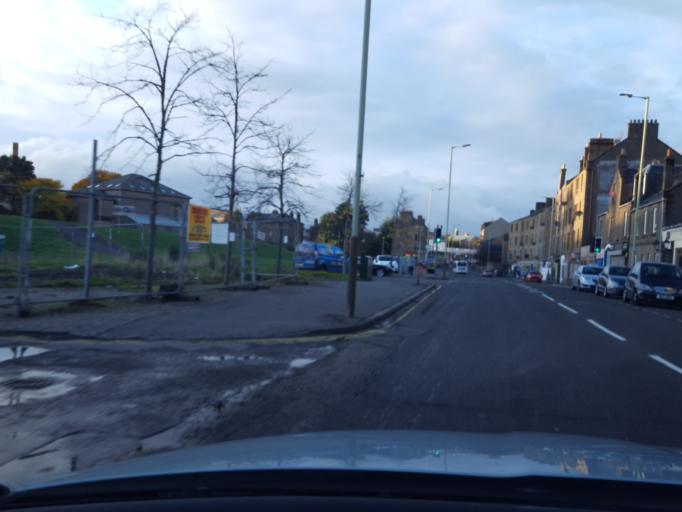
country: GB
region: Scotland
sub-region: Dundee City
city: Dundee
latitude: 56.4722
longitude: -2.9771
